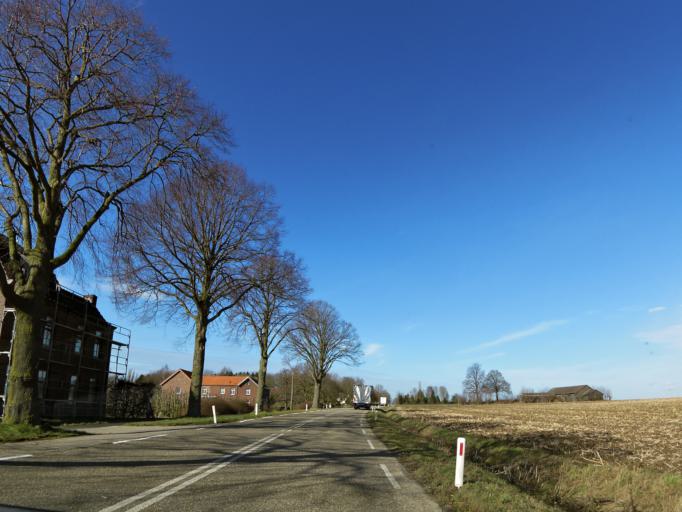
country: NL
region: Limburg
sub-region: Eijsden-Margraten
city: Margraten
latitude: 50.7808
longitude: 5.8357
